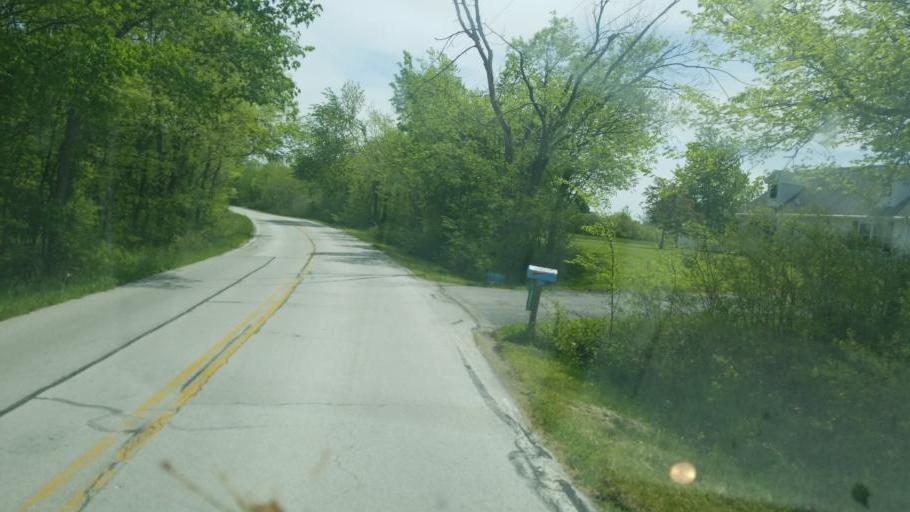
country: US
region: Ohio
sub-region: Ottawa County
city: Oak Harbor
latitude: 41.4947
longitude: -83.1999
